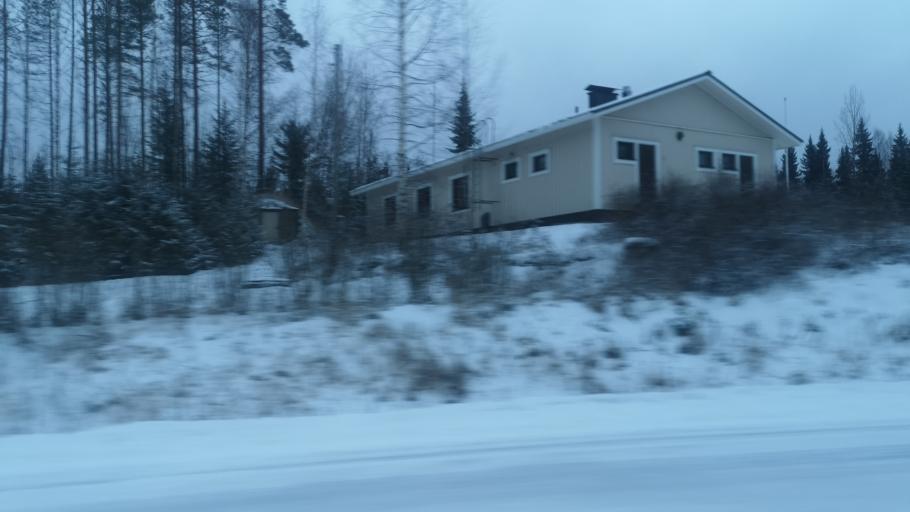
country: FI
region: Southern Savonia
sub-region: Savonlinna
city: Enonkoski
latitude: 62.0574
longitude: 28.7151
